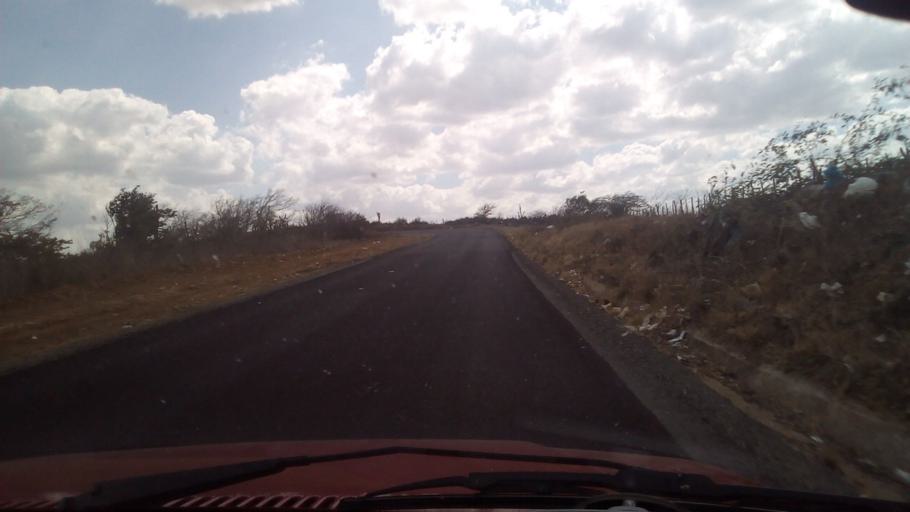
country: BR
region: Paraiba
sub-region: Bananeiras
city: Bananeiras
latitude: -6.7388
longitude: -35.7179
